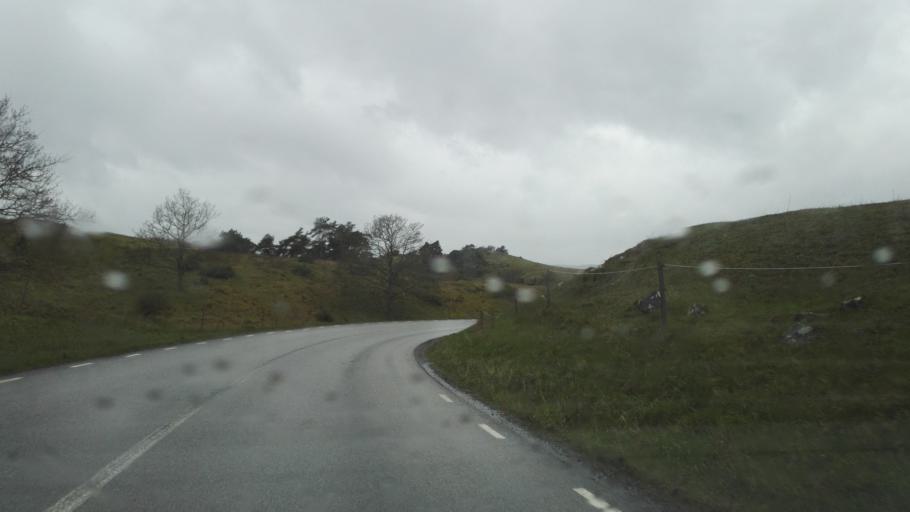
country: SE
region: Skane
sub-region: Kristianstads Kommun
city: Degeberga
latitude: 55.7215
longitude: 14.1193
